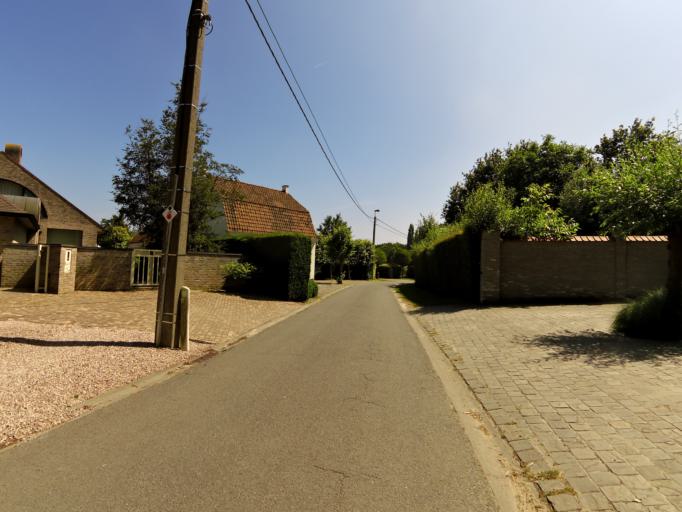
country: BE
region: Flanders
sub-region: Provincie West-Vlaanderen
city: Zedelgem
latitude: 51.1561
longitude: 3.1572
